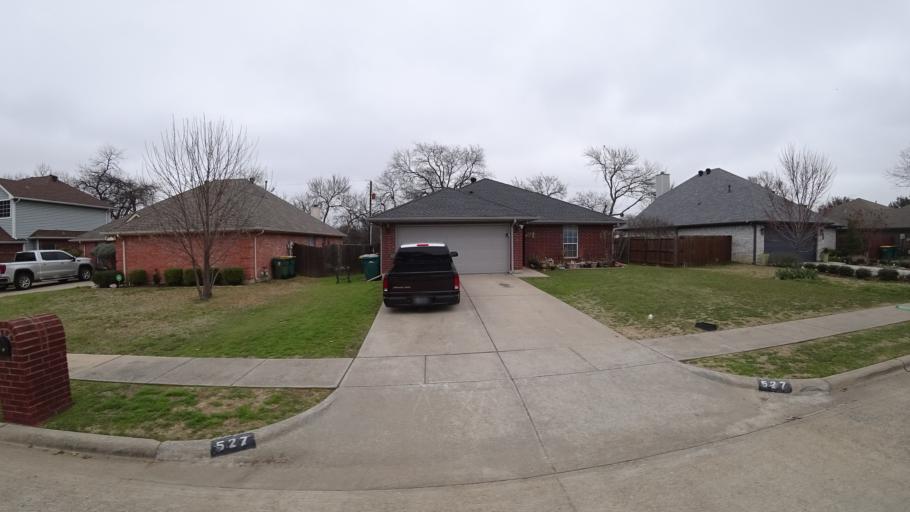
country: US
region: Texas
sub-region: Denton County
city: Lewisville
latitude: 33.0561
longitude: -97.0053
